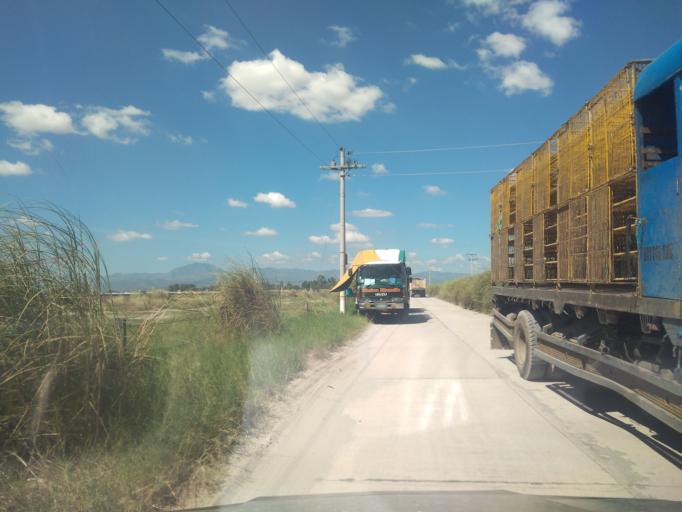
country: PH
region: Central Luzon
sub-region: Province of Pampanga
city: Balas
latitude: 15.0589
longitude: 120.5968
